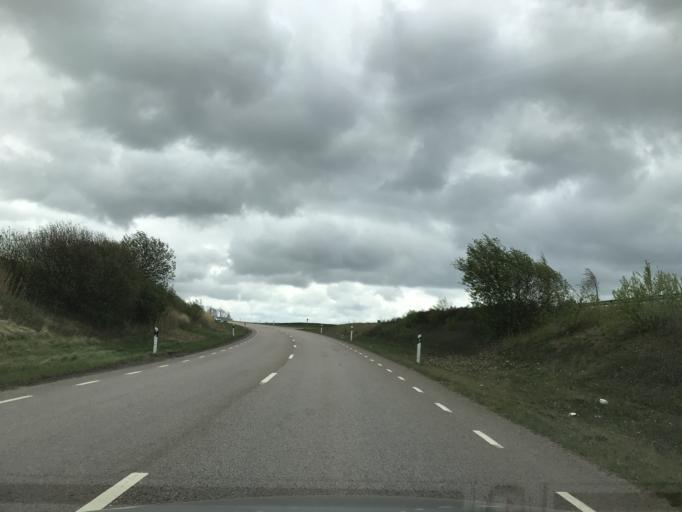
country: SE
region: Skane
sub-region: Helsingborg
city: Glumslov
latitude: 55.9551
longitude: 12.7948
